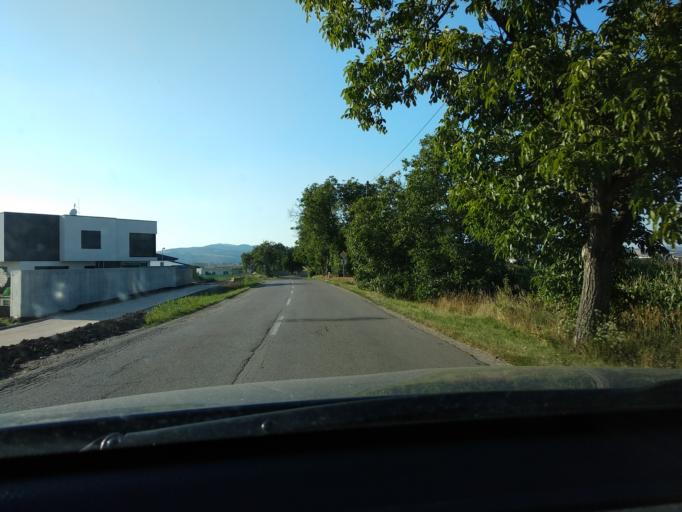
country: SK
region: Trenciansky
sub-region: Okres Trencin
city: Trencin
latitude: 48.8556
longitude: 18.0184
